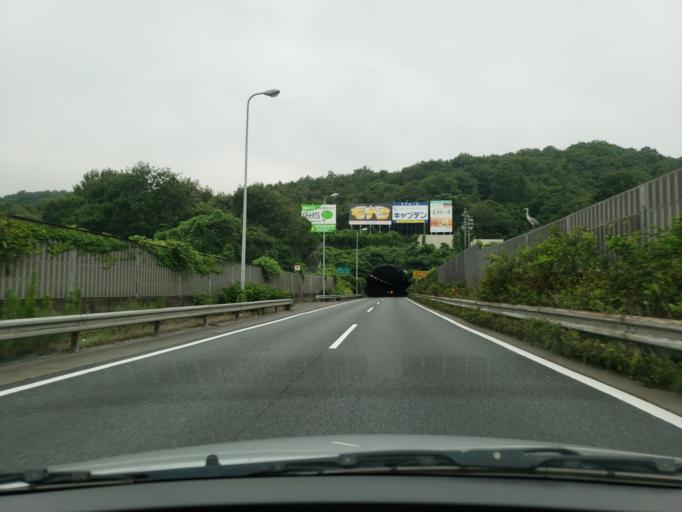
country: JP
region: Hyogo
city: Himeji
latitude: 34.8185
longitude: 134.6456
